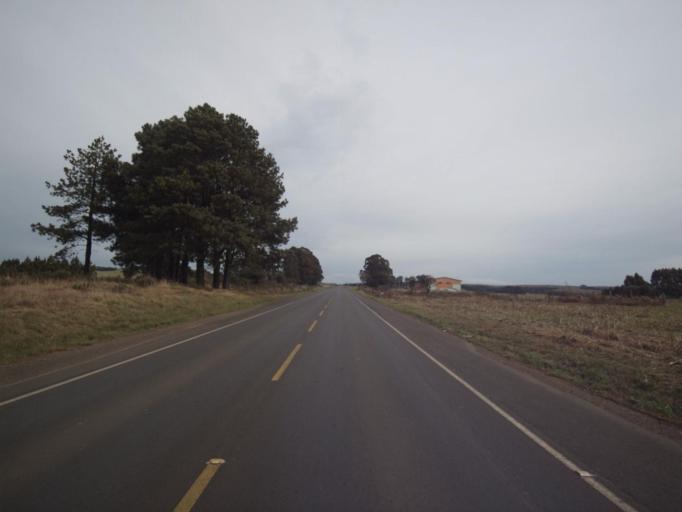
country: BR
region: Parana
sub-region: Palmas
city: Palmas
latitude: -26.7744
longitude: -51.6793
